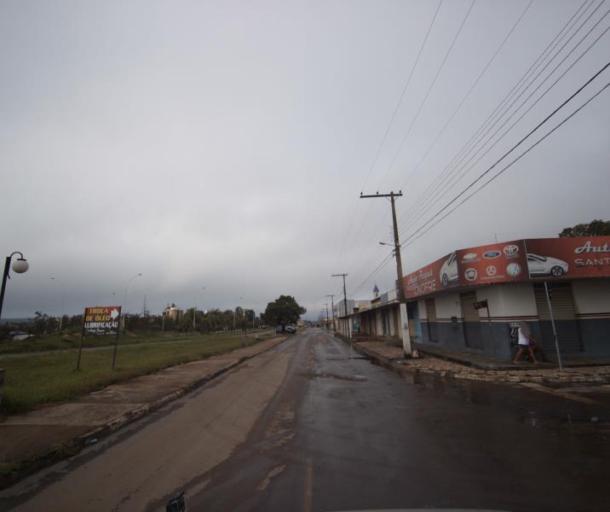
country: BR
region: Goias
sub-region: Pirenopolis
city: Pirenopolis
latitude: -15.7833
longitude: -48.7689
